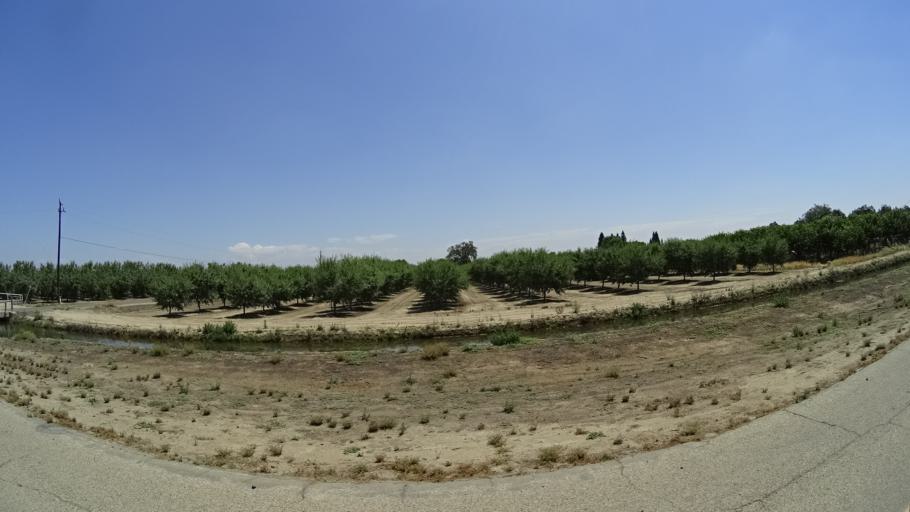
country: US
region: California
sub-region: Fresno County
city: Kingsburg
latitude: 36.4960
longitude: -119.5389
